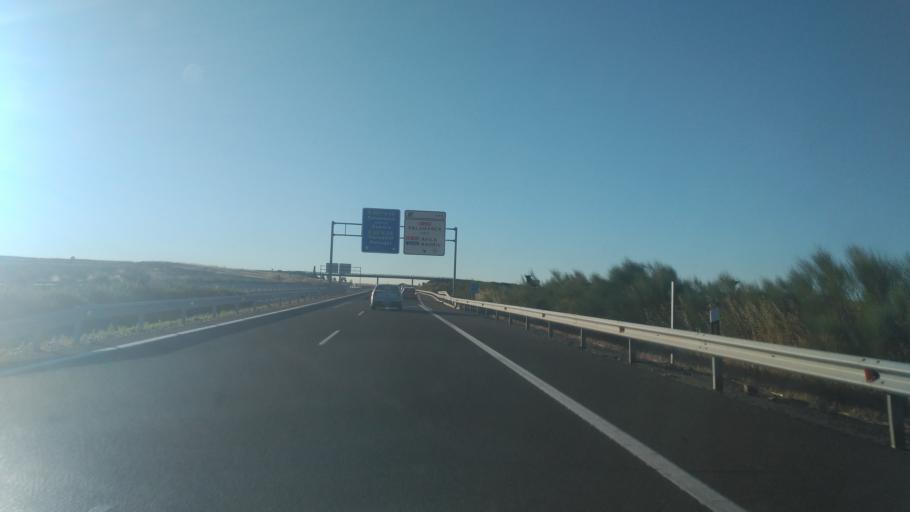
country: ES
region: Castille and Leon
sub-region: Provincia de Salamanca
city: Carbajosa de la Sagrada
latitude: 40.9185
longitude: -5.6640
